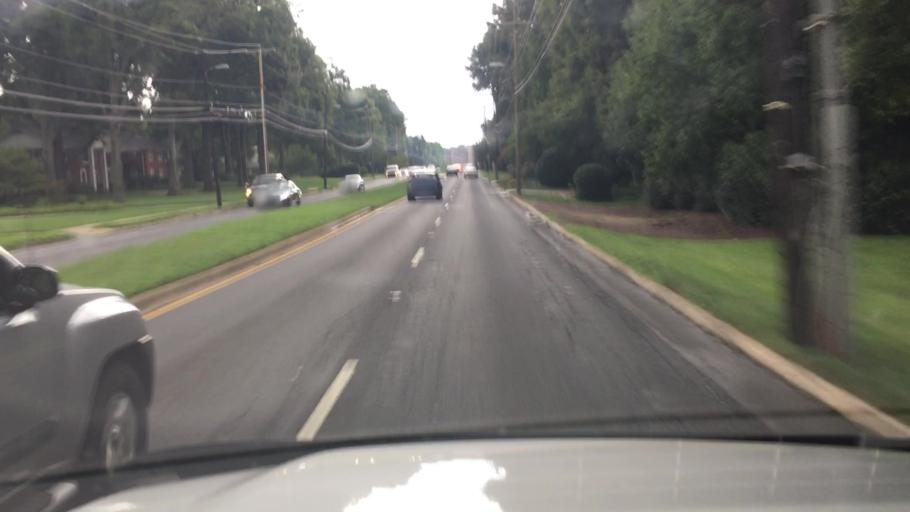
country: US
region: North Carolina
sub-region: Mecklenburg County
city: Charlotte
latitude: 35.1643
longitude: -80.8024
